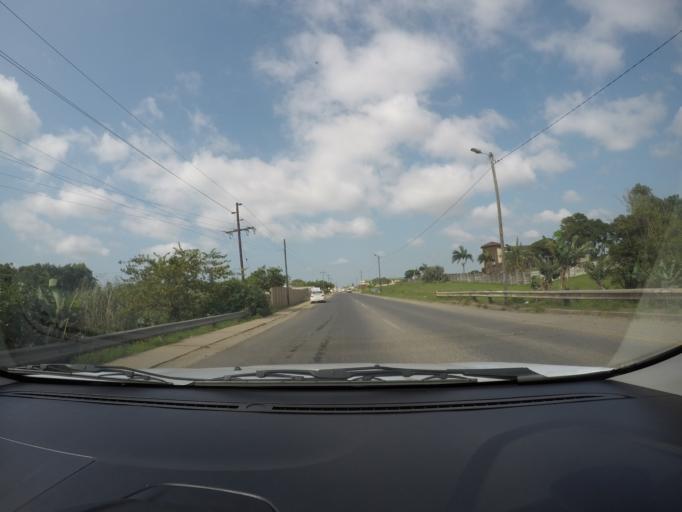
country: ZA
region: KwaZulu-Natal
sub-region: uThungulu District Municipality
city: eSikhawini
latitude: -28.8805
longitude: 31.9078
